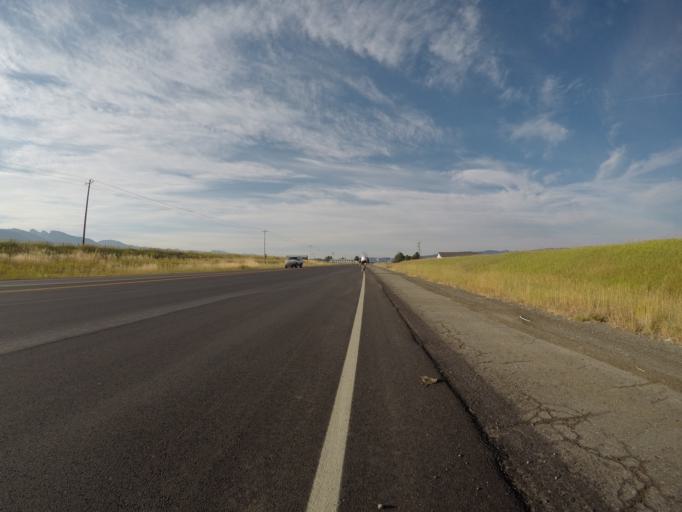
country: US
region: Wyoming
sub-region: Lincoln County
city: Afton
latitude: 42.9812
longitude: -111.0125
